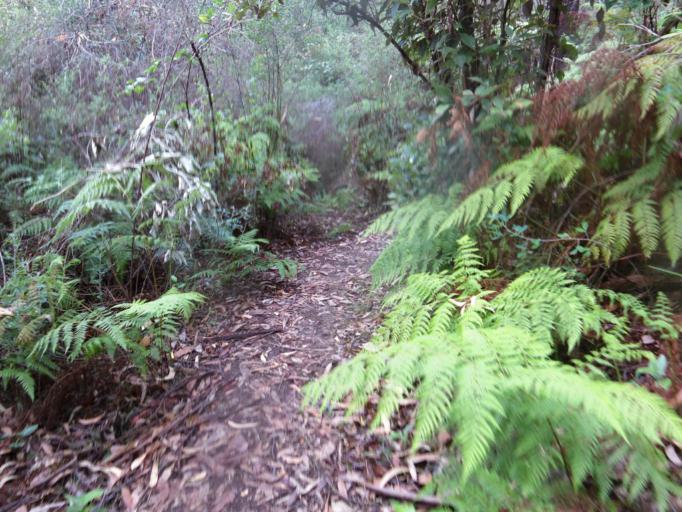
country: AU
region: Victoria
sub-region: Nillumbik
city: Saint Andrews
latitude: -37.5415
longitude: 145.3481
